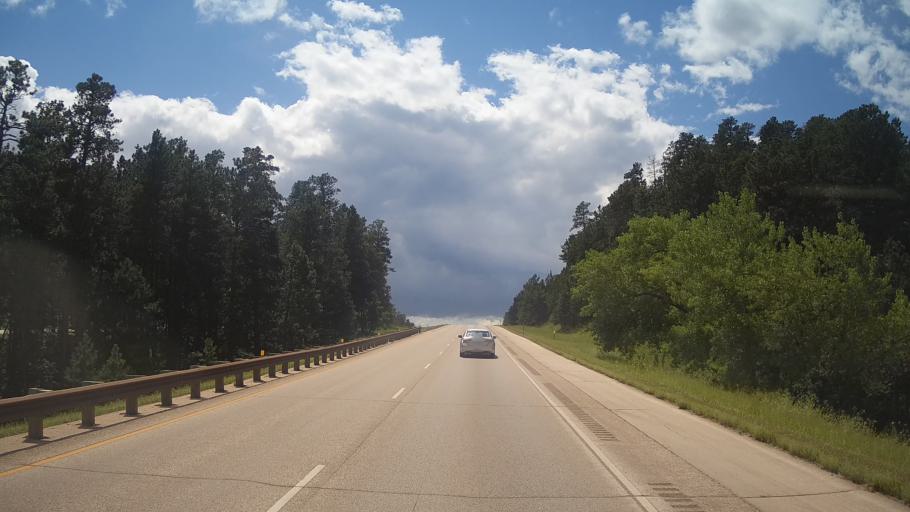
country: US
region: South Dakota
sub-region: Pennington County
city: Colonial Pine Hills
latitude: 43.9488
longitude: -103.3697
